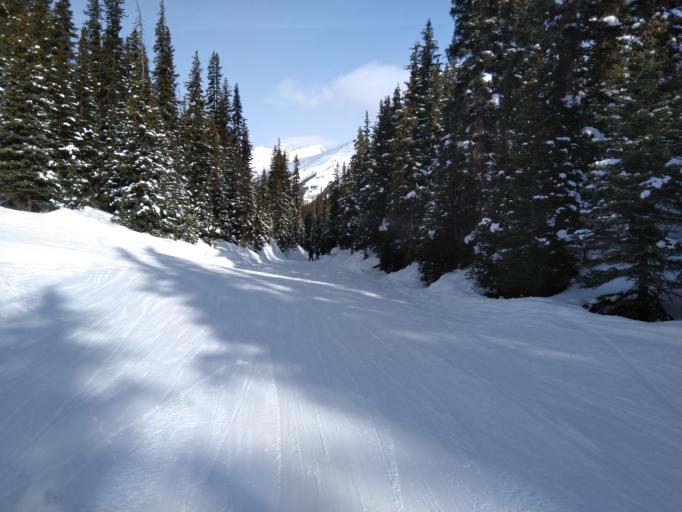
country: CA
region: Alberta
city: Banff
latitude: 51.0902
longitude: -115.7685
